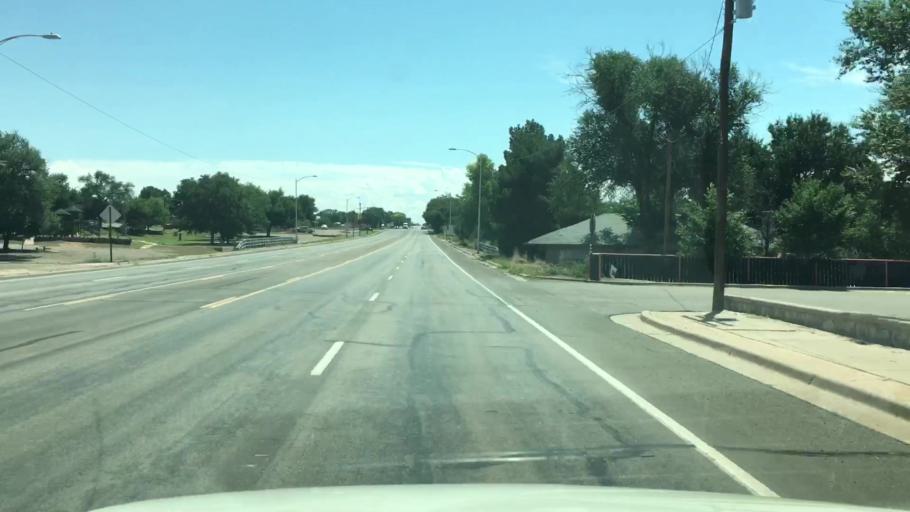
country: US
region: New Mexico
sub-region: De Baca County
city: Fort Sumner
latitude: 34.4689
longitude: -104.2367
